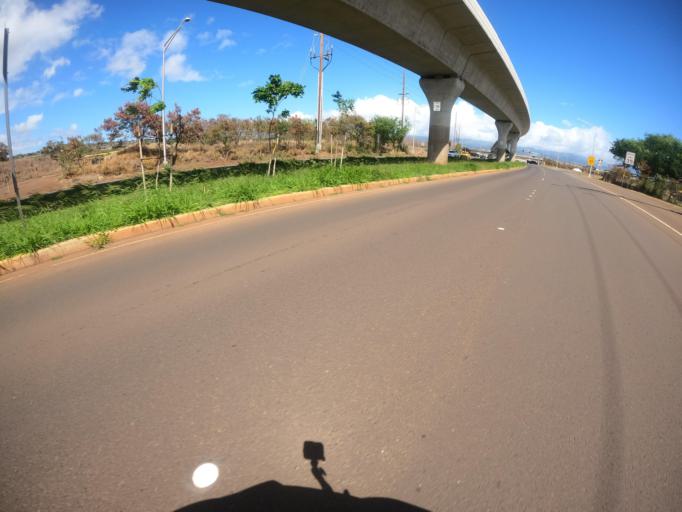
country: US
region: Hawaii
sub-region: Honolulu County
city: Royal Kunia
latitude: 21.3747
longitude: -158.0297
